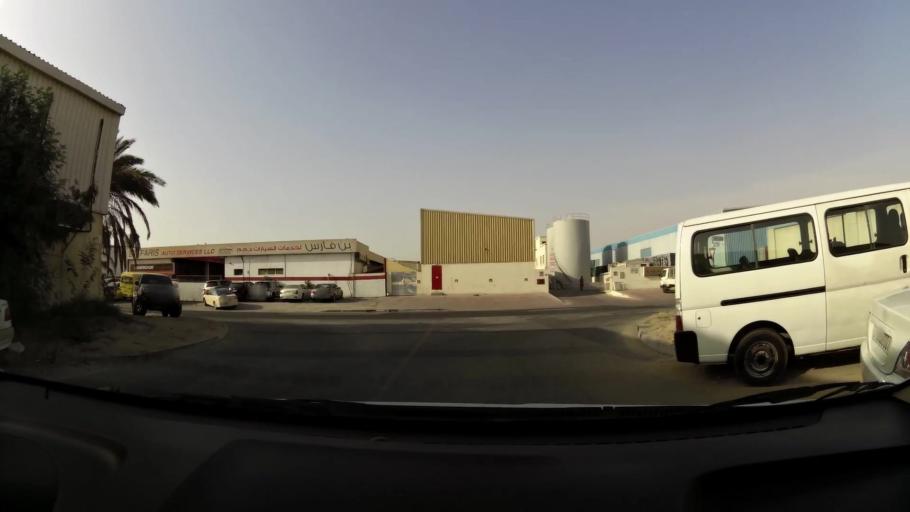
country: AE
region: Ash Shariqah
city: Sharjah
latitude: 25.2330
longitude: 55.3737
